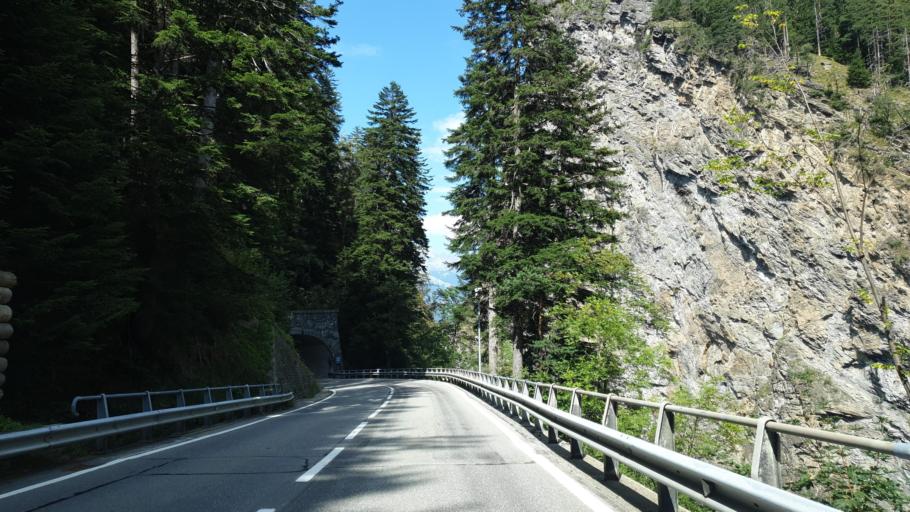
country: CH
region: Grisons
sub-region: Hinterrhein District
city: Thusis
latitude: 46.6881
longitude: 9.4439
